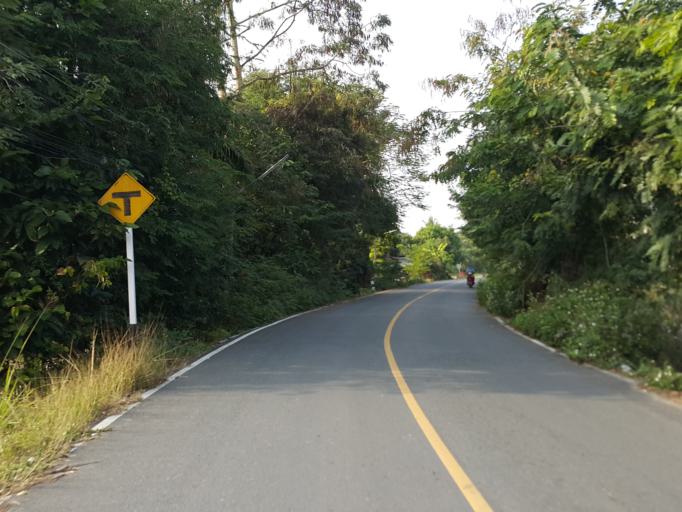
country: TH
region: Chiang Mai
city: San Sai
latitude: 18.8681
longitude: 99.1385
